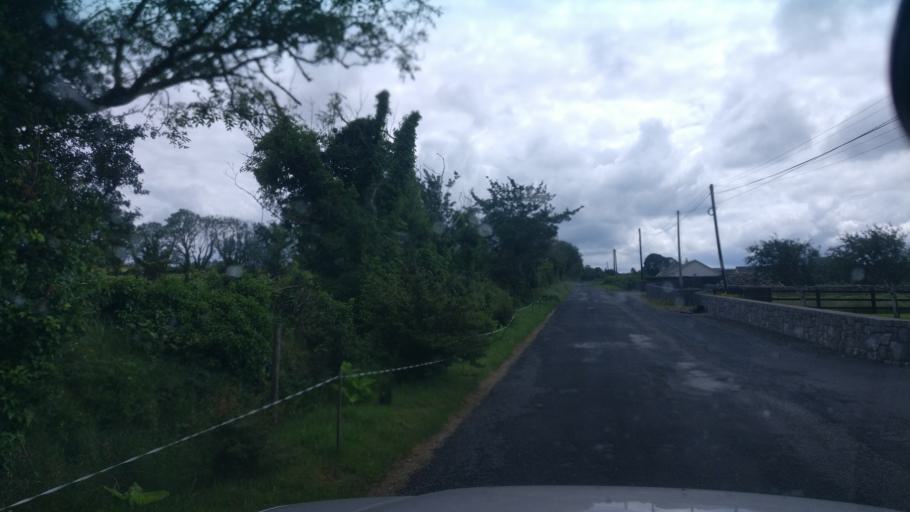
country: IE
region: Connaught
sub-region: County Galway
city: Loughrea
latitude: 53.1615
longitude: -8.5724
